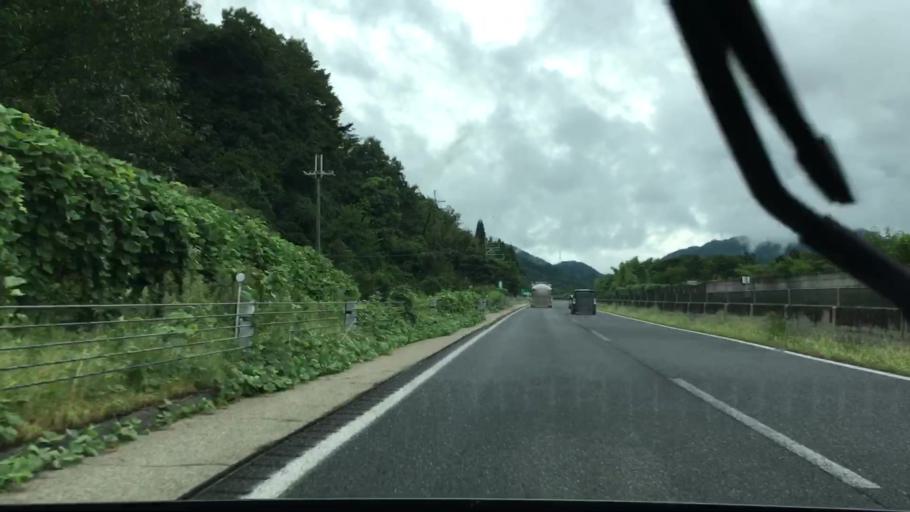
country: JP
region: Hyogo
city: Yamazakicho-nakabirose
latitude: 35.0175
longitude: 134.5061
